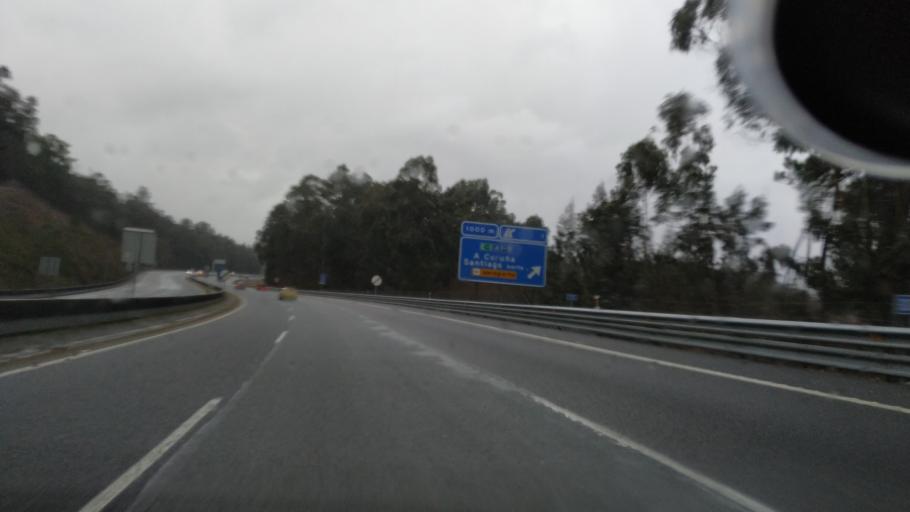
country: ES
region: Galicia
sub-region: Provincia da Coruna
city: Santiago de Compostela
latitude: 42.8426
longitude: -8.5299
